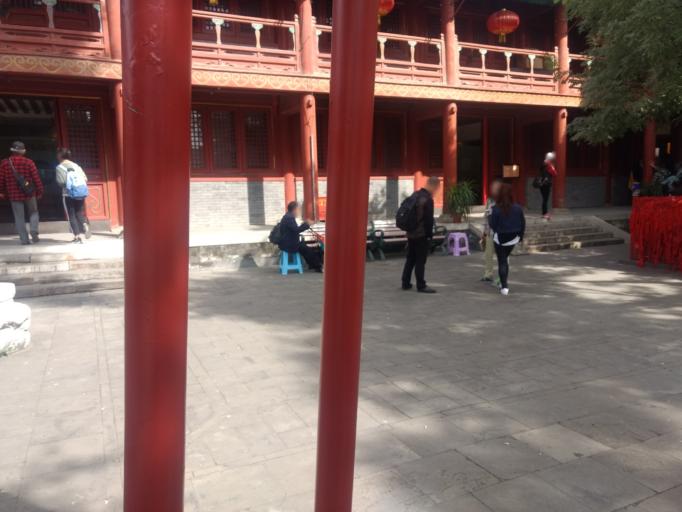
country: CN
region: Beijing
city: Chaowai
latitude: 39.9243
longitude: 116.4380
